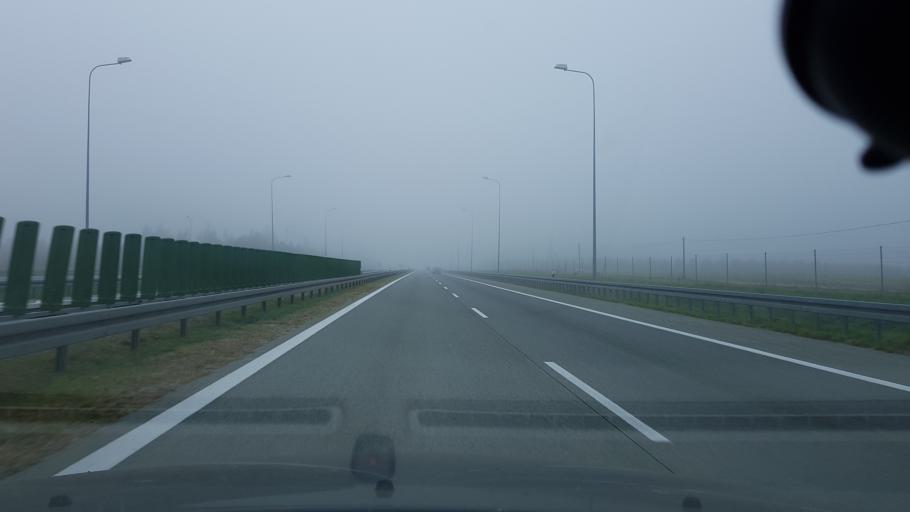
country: PL
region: Lodz Voivodeship
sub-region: Powiat skierniewicki
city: Kowiesy
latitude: 51.8625
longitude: 20.3817
